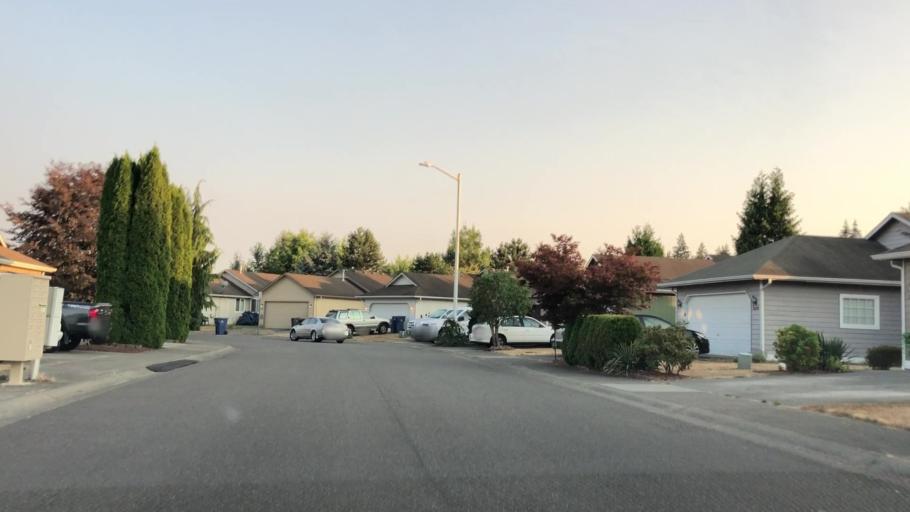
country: US
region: Washington
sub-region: Snohomish County
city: Marysville
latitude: 48.0877
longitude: -122.1504
